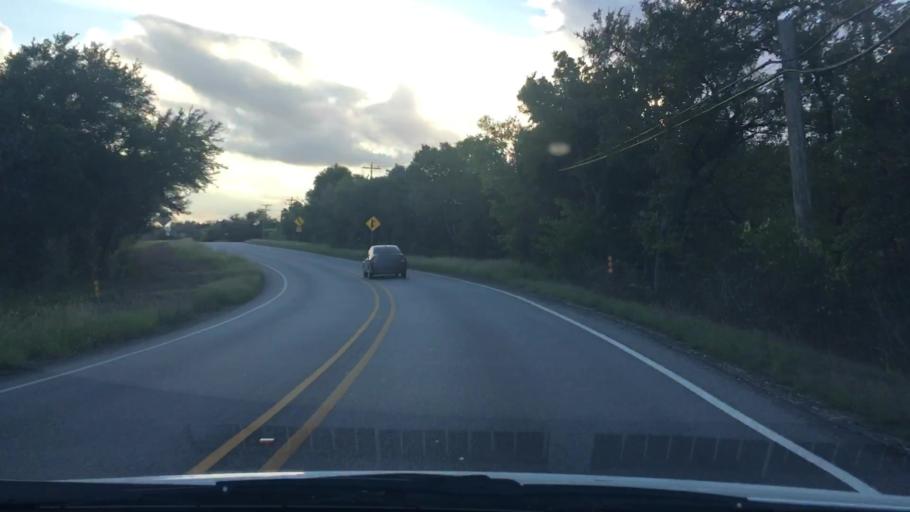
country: US
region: Texas
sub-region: Williamson County
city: Anderson Mill
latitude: 30.4587
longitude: -97.8439
